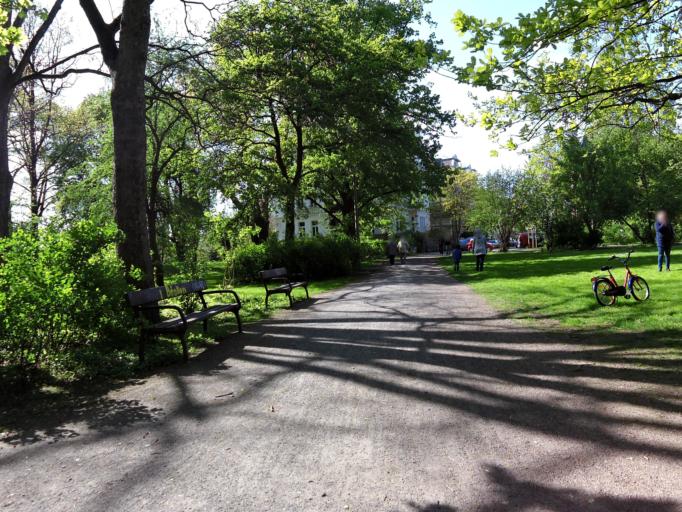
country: DE
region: Saxony
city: Leipzig
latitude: 51.3576
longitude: 12.3581
